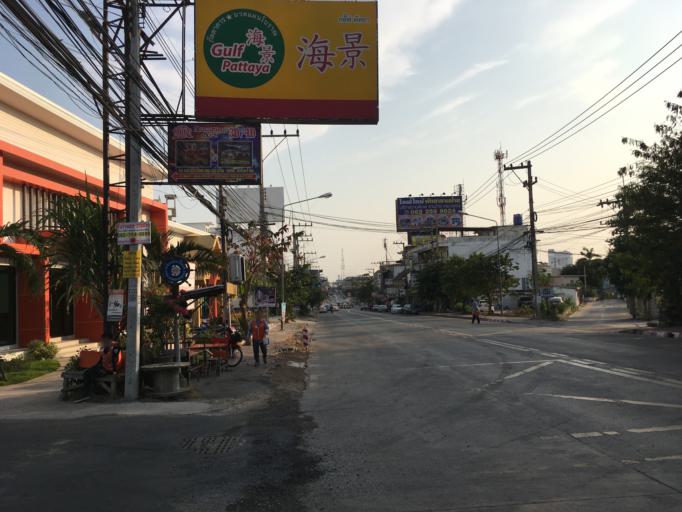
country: TH
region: Chon Buri
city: Phatthaya
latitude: 12.9445
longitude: 100.8956
